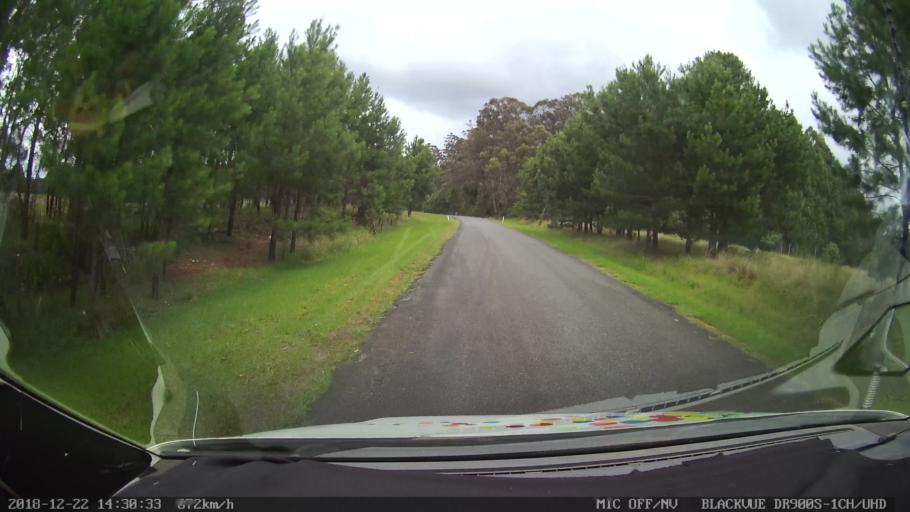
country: AU
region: New South Wales
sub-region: Bellingen
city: Dorrigo
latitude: -30.0879
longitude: 152.6313
